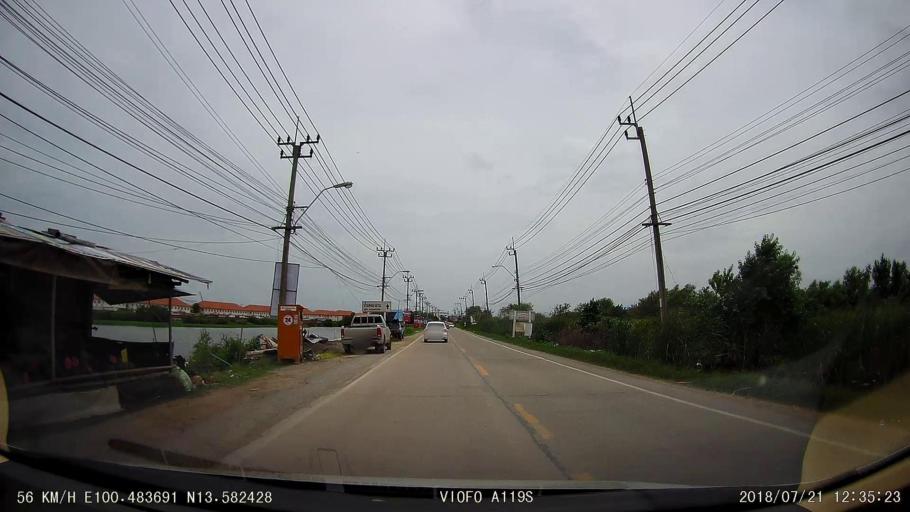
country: TH
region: Bangkok
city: Thung Khru
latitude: 13.5824
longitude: 100.4836
